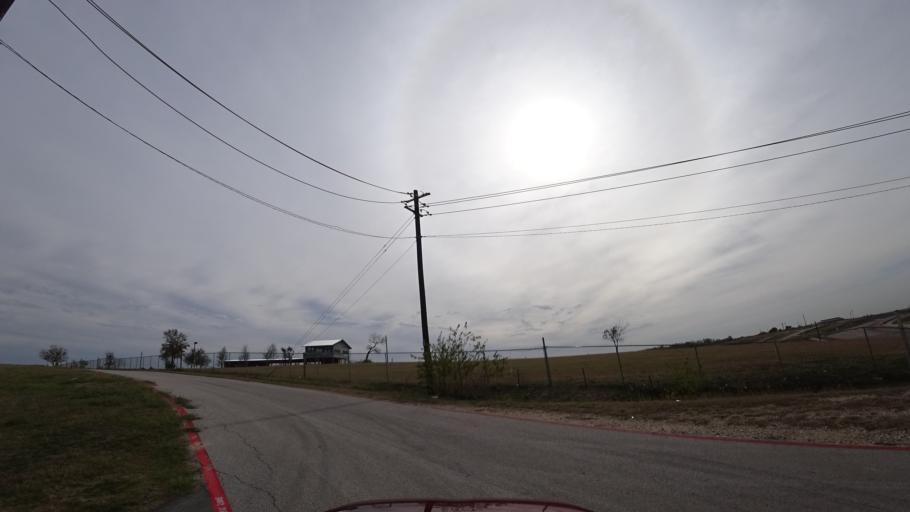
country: US
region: Texas
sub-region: Travis County
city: Garfield
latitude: 30.1388
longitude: -97.6234
